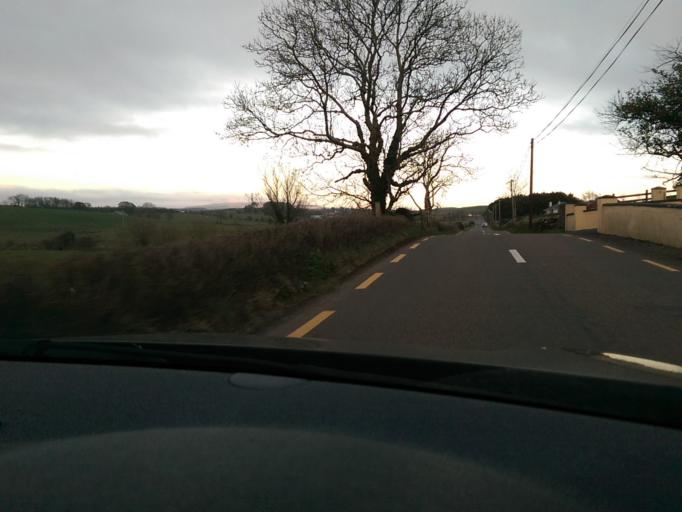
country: IE
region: Connaught
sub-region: Sligo
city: Ballymote
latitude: 53.9866
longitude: -8.4824
